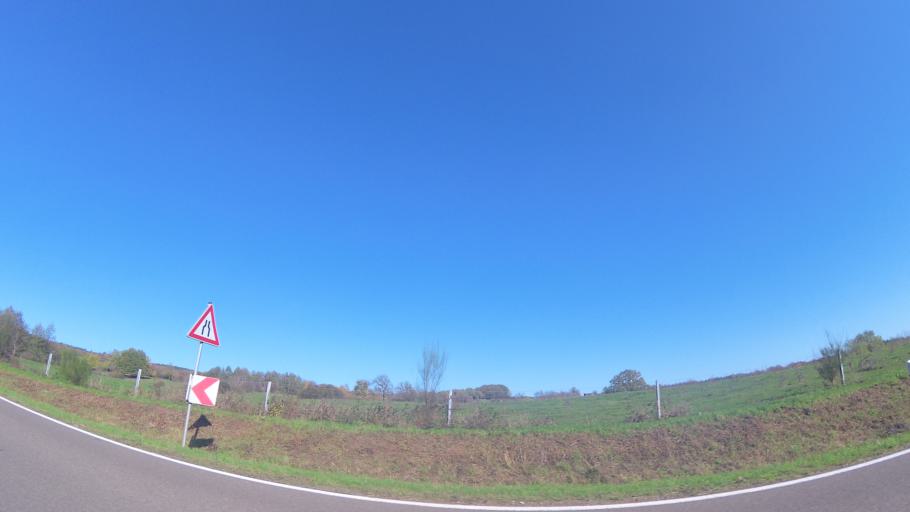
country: DE
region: Saarland
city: Britten
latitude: 49.5271
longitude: 6.7016
